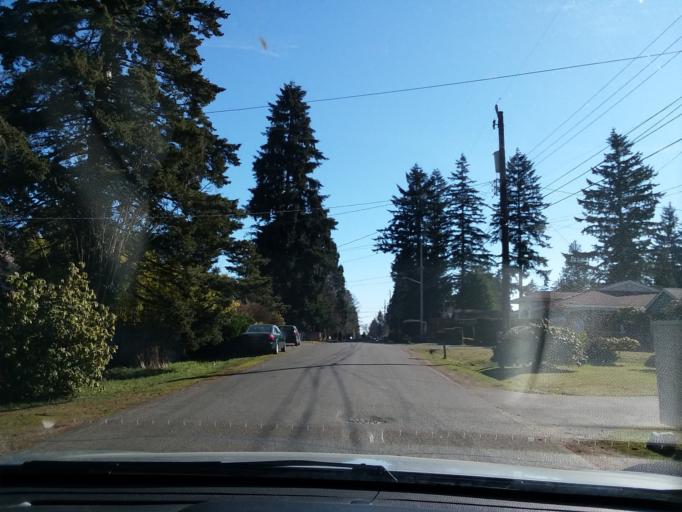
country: US
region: Washington
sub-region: King County
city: Shoreline
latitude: 47.7314
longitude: -122.3316
